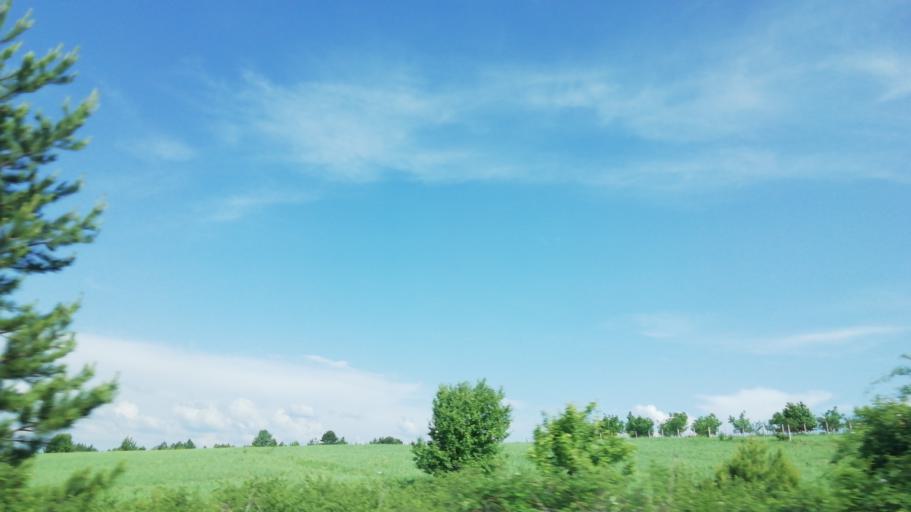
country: TR
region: Karabuk
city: Karabuk
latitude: 41.0911
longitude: 32.5882
